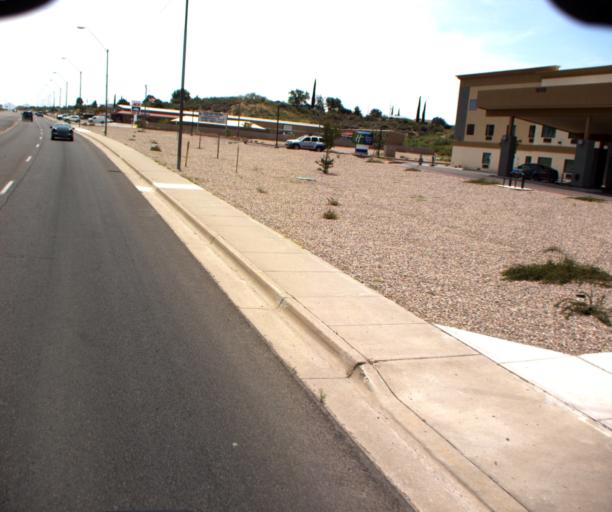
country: US
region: Arizona
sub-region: Gila County
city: Globe
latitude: 33.3883
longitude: -110.7612
